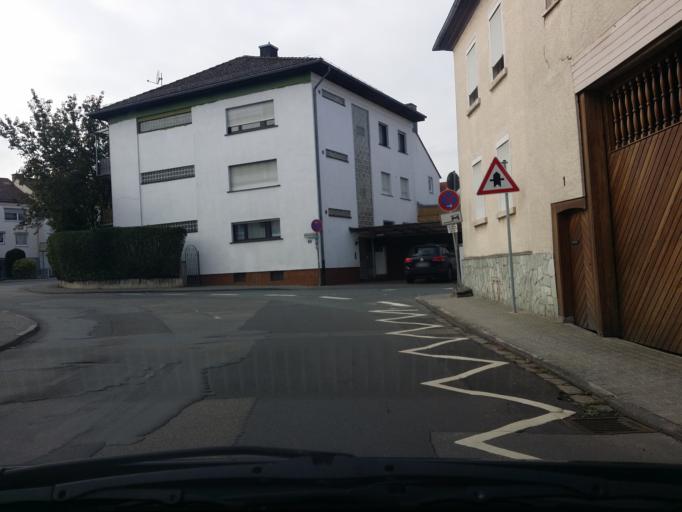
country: DE
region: Hesse
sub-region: Regierungsbezirk Darmstadt
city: Eschborn
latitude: 50.1413
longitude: 8.5684
